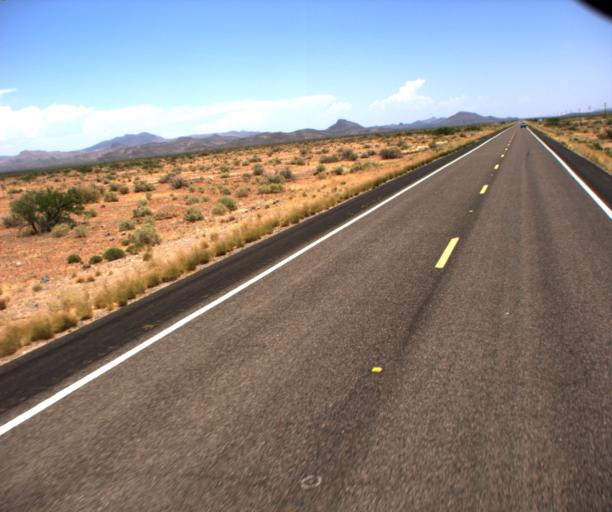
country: US
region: Arizona
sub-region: Graham County
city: Safford
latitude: 32.7741
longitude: -109.4976
